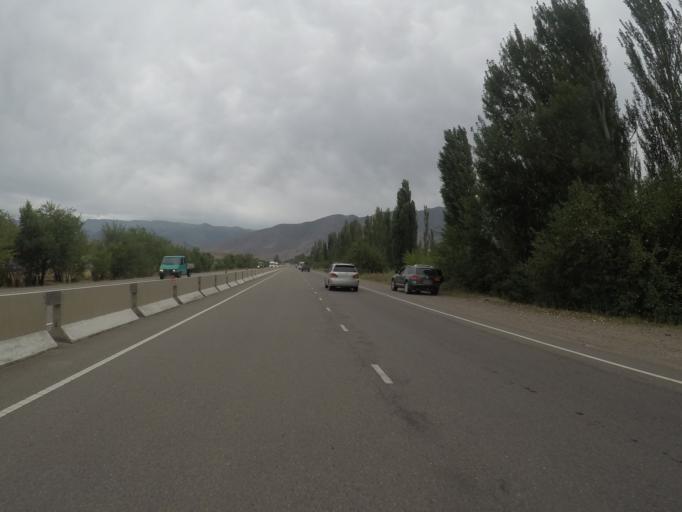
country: KG
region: Chuy
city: Bystrovka
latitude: 42.7438
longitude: 75.8333
